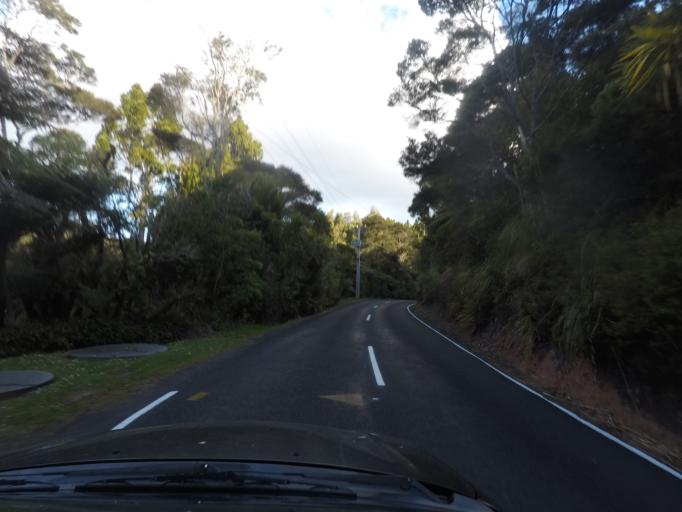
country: NZ
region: Auckland
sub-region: Auckland
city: Titirangi
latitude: -36.9349
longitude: 174.6186
